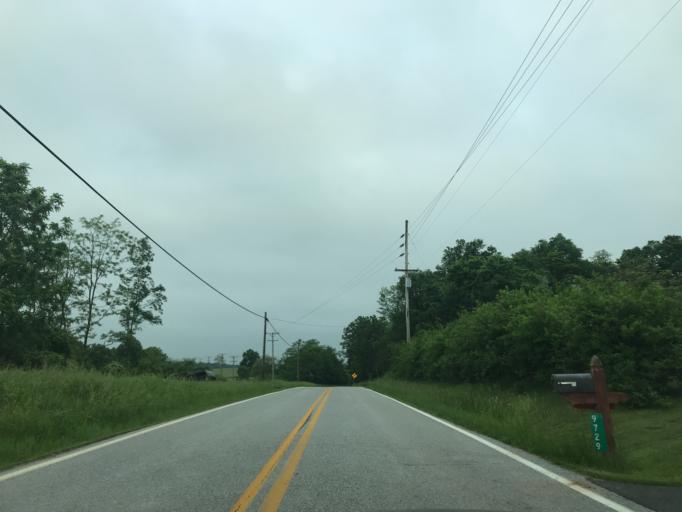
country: US
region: Maryland
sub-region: Frederick County
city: Emmitsburg
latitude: 39.6870
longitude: -77.3283
